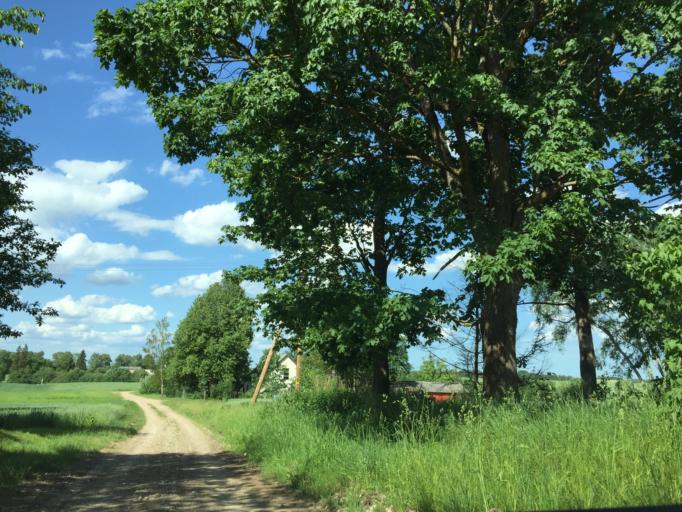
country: LV
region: Tukuma Rajons
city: Tukums
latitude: 56.8802
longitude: 23.0764
